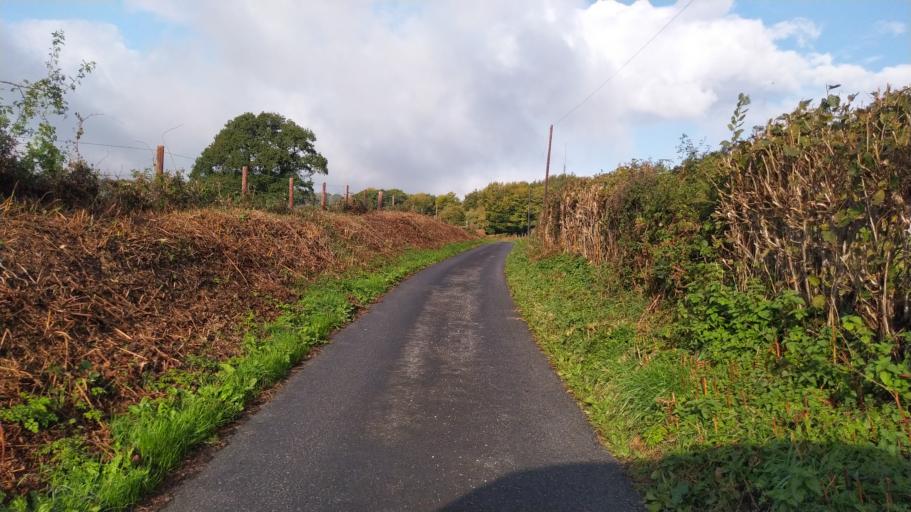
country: GB
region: England
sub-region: Dorset
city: Shaftesbury
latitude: 51.0282
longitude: -2.1355
